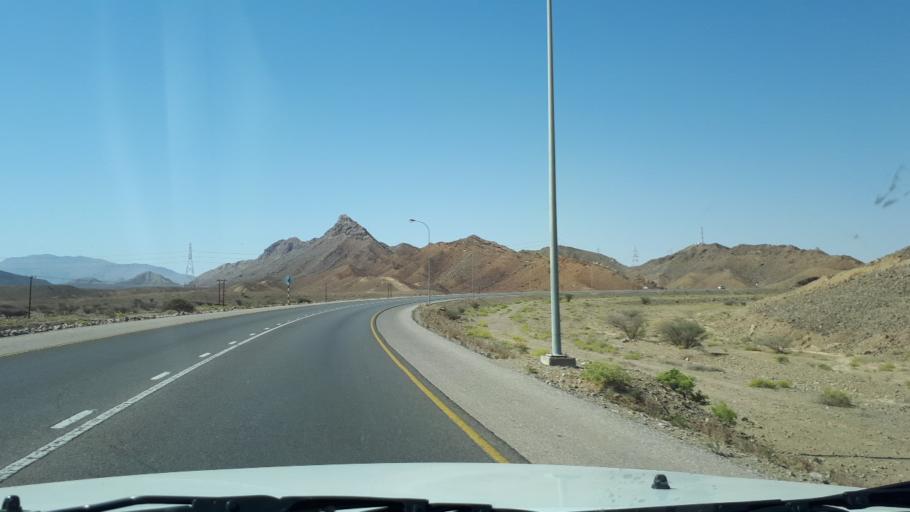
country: OM
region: Ash Sharqiyah
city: Sur
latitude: 22.3421
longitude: 59.3147
